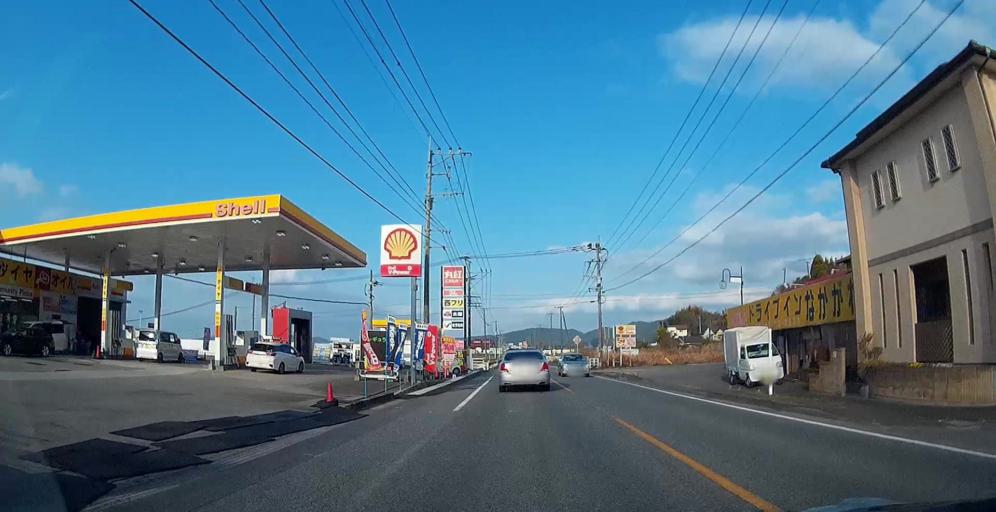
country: JP
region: Kumamoto
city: Matsubase
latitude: 32.5790
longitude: 130.6967
